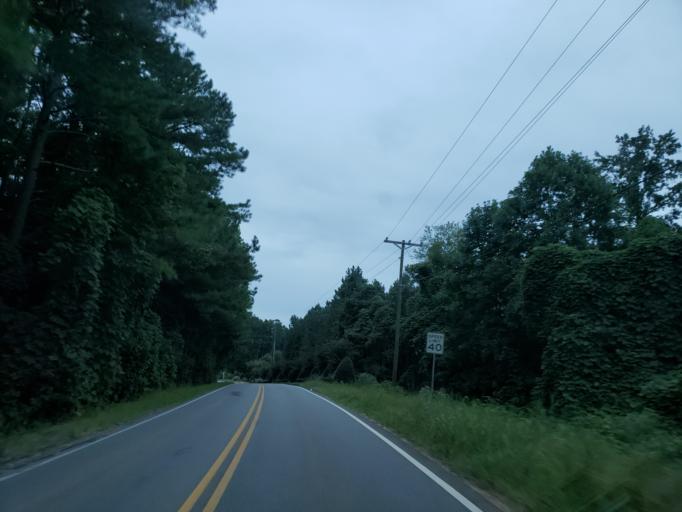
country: US
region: Georgia
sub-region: Cherokee County
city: Canton
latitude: 34.2871
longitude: -84.4540
